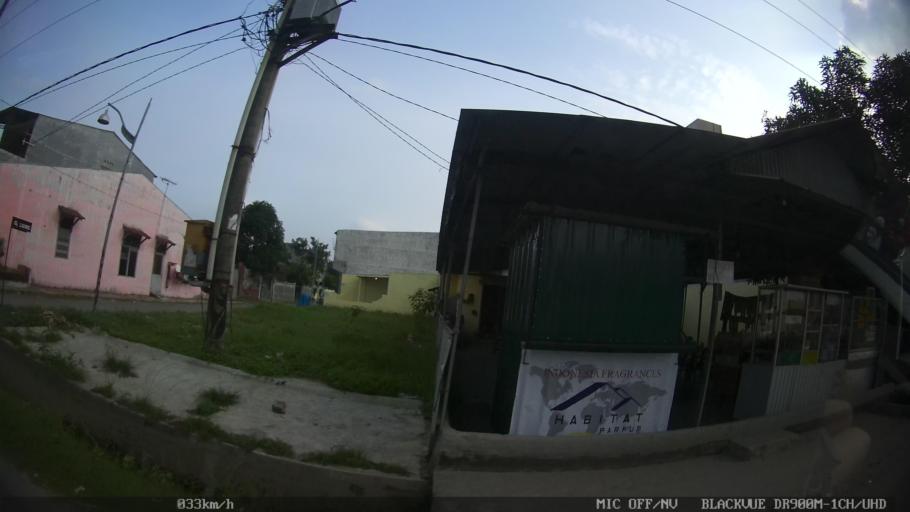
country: ID
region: North Sumatra
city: Medan
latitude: 3.5814
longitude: 98.7347
